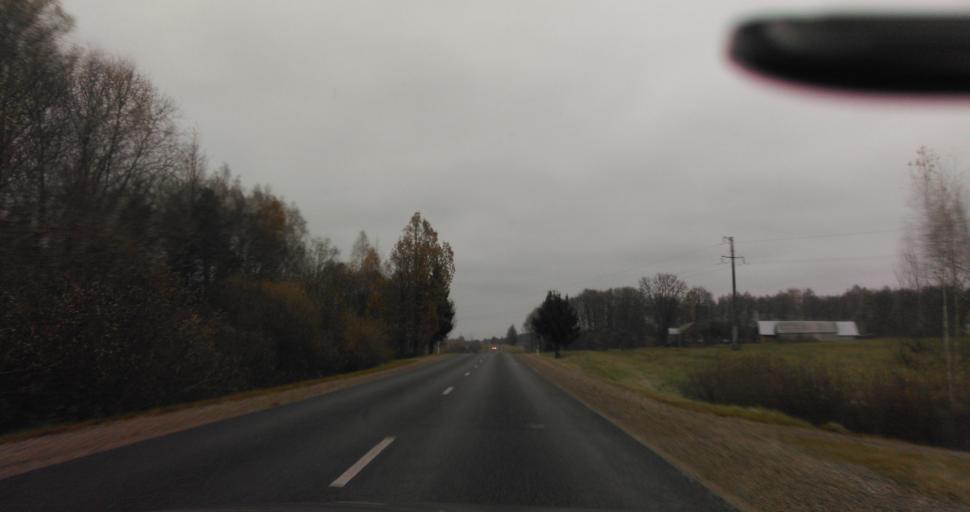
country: LT
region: Panevezys
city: Rokiskis
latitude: 55.8909
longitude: 25.5494
